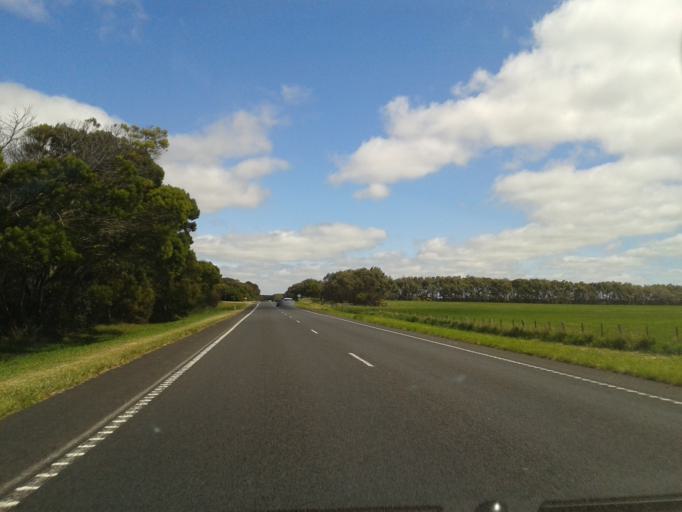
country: AU
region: Victoria
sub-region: Glenelg
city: Portland
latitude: -38.2520
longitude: 141.9094
